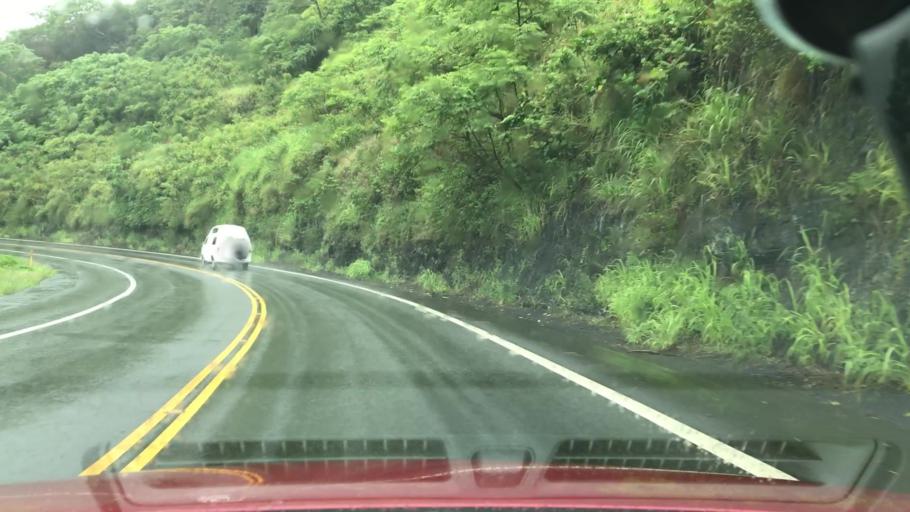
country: US
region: Hawaii
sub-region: Hawaii County
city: Pepeekeo
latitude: 19.9883
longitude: -155.2490
